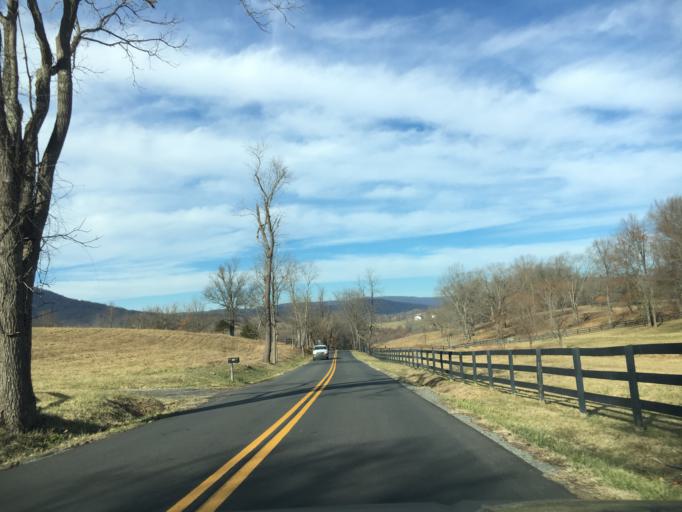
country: US
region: Virginia
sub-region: Warren County
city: Apple Mountain Lake
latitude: 38.8432
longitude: -77.9962
